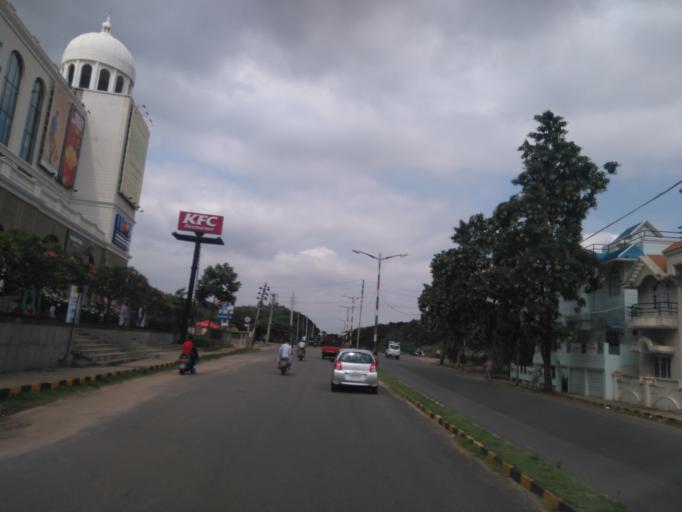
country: IN
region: Karnataka
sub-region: Mysore
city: Mysore
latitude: 12.2984
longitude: 76.6648
